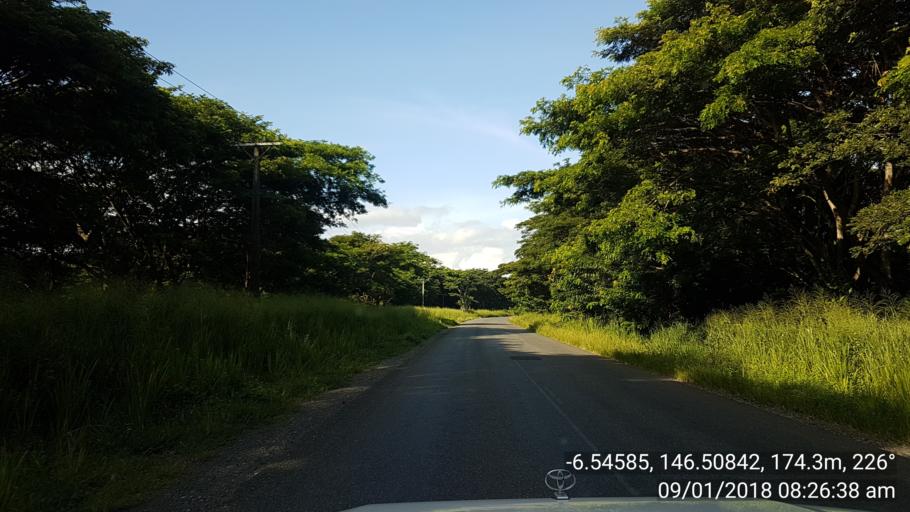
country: PG
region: Morobe
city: Lae
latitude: -6.5458
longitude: 146.5083
